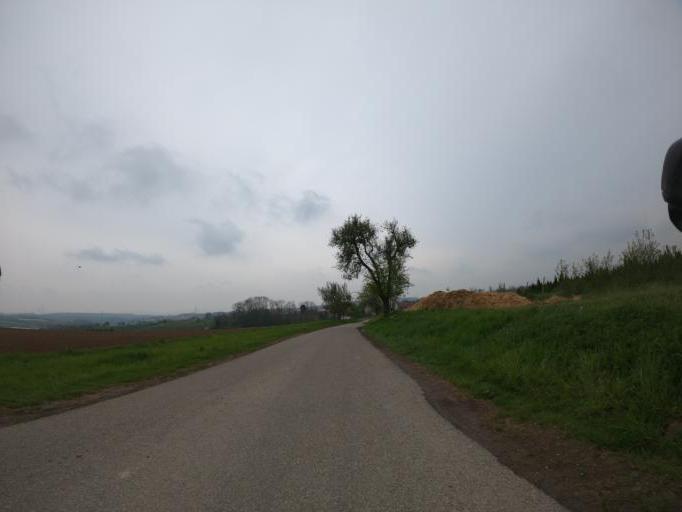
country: DE
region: Baden-Wuerttemberg
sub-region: Regierungsbezirk Stuttgart
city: Markgroningen
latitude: 48.8923
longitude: 9.0782
